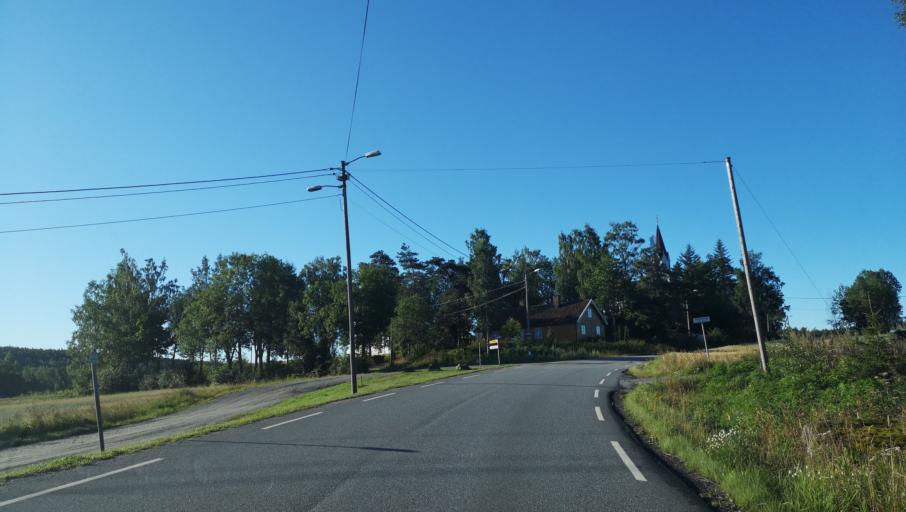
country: NO
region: Ostfold
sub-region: Hobol
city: Tomter
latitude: 59.6528
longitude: 11.0102
